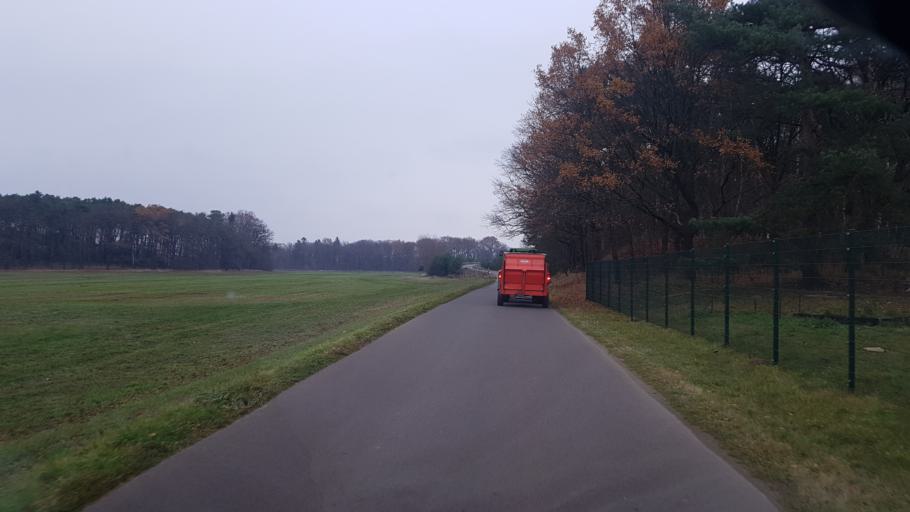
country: DE
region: Brandenburg
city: Schenkendobern
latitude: 51.9607
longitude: 14.6431
